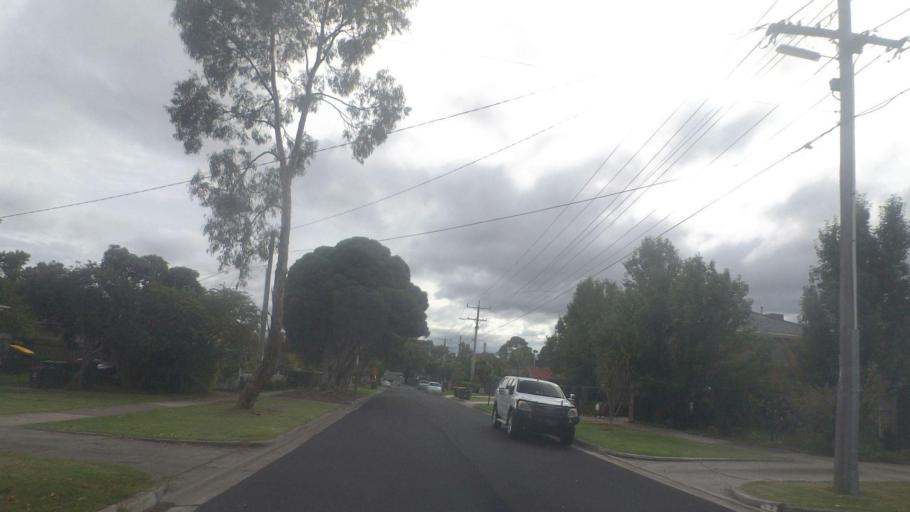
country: AU
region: Victoria
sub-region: Whitehorse
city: Blackburn South
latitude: -37.8333
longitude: 145.1475
